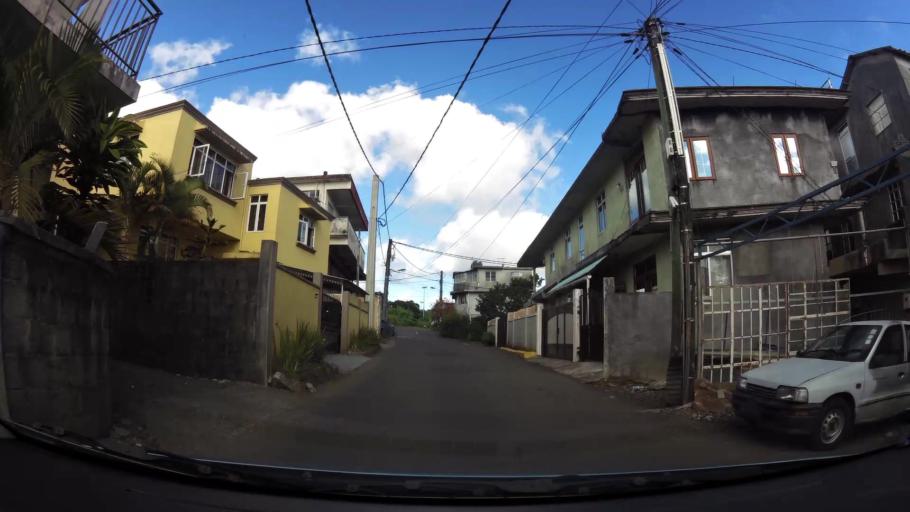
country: MU
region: Plaines Wilhems
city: Curepipe
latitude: -20.3074
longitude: 57.5181
